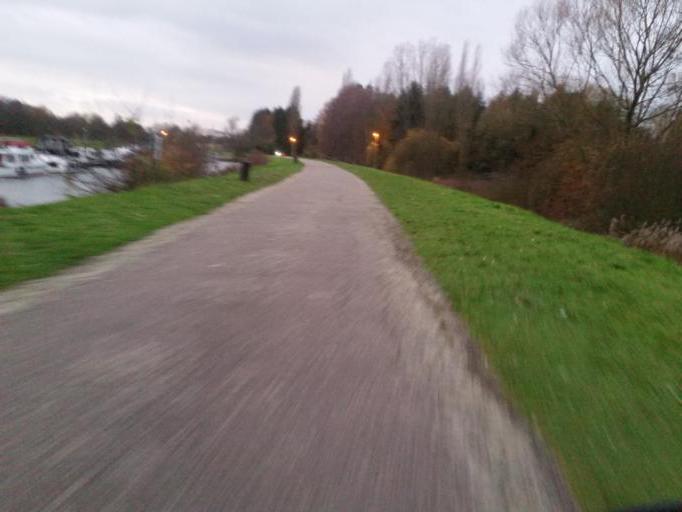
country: BE
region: Flanders
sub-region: Provincie Antwerpen
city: Lier
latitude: 51.1513
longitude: 4.5841
